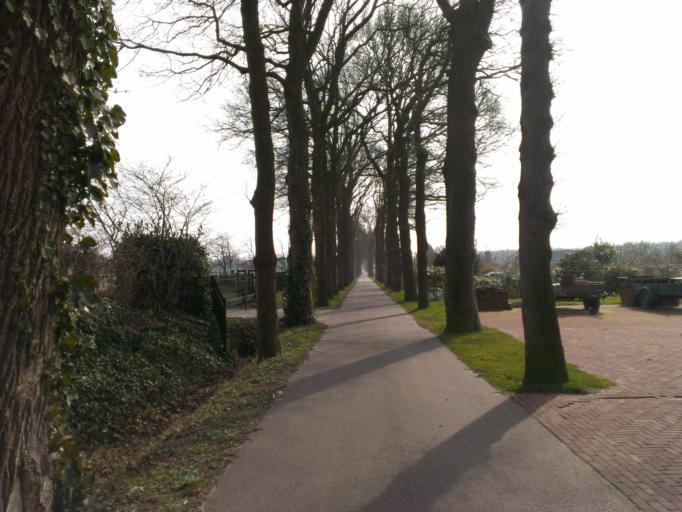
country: NL
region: Drenthe
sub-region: Gemeente Hoogeveen
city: Hoogeveen
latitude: 52.7478
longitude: 6.5013
